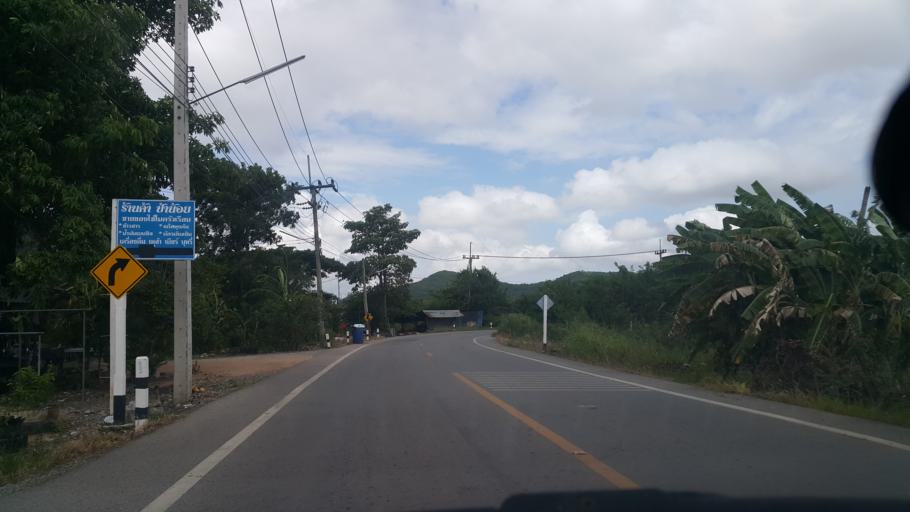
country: TH
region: Rayong
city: Ban Chang
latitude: 12.7604
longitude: 100.9595
